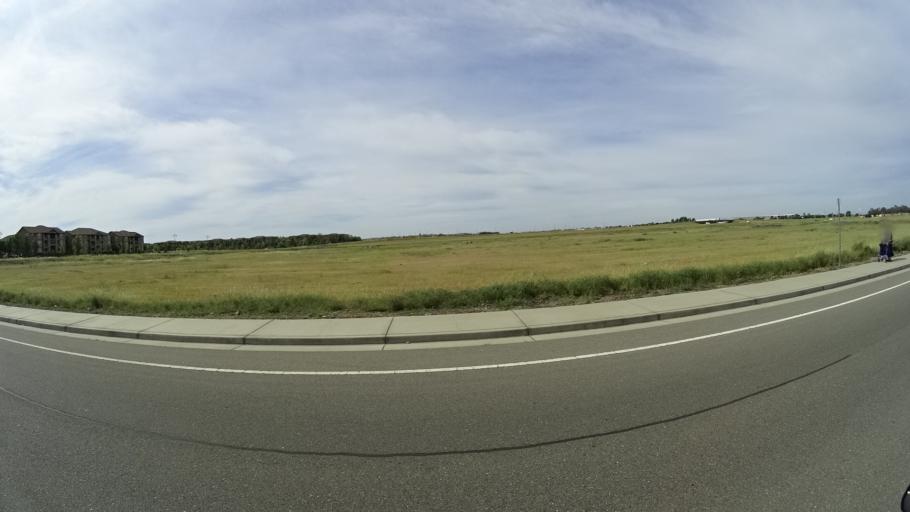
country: US
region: California
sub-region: Placer County
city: Lincoln
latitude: 38.8377
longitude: -121.2943
